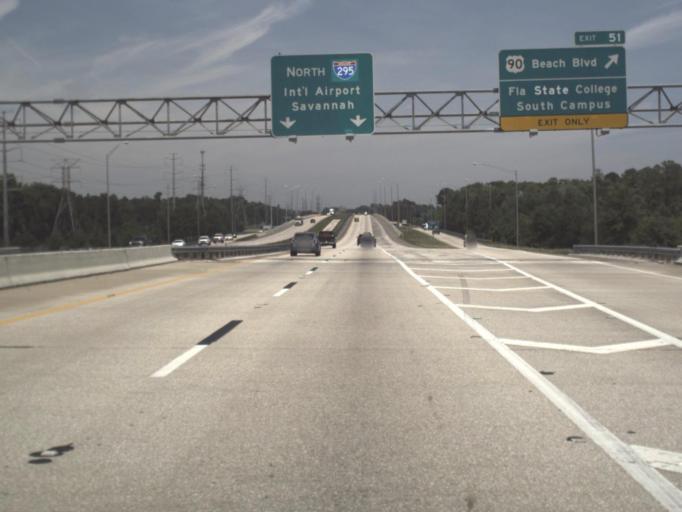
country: US
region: Florida
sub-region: Duval County
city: Neptune Beach
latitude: 30.2816
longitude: -81.5215
